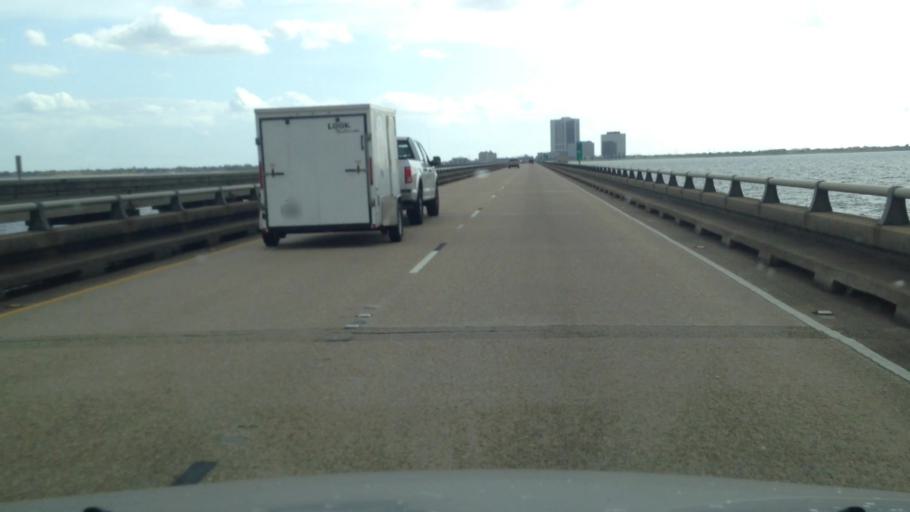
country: US
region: Louisiana
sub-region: Jefferson Parish
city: Metairie
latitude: 30.0425
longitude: -90.1504
